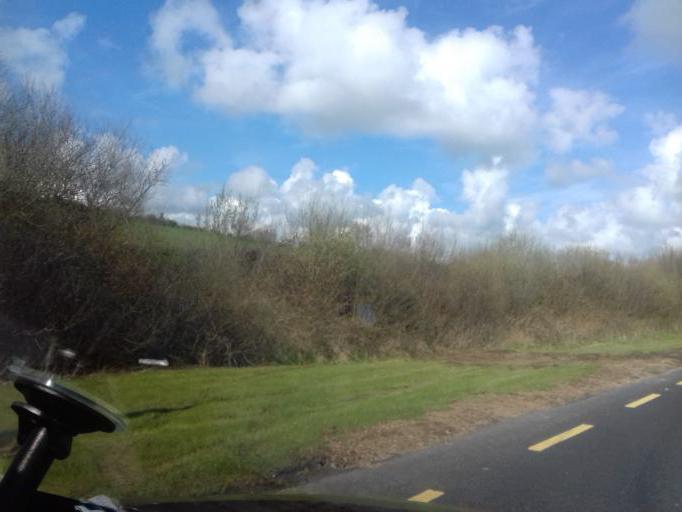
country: IE
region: Ulster
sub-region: An Cabhan
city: Cavan
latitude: 53.9874
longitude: -7.2586
